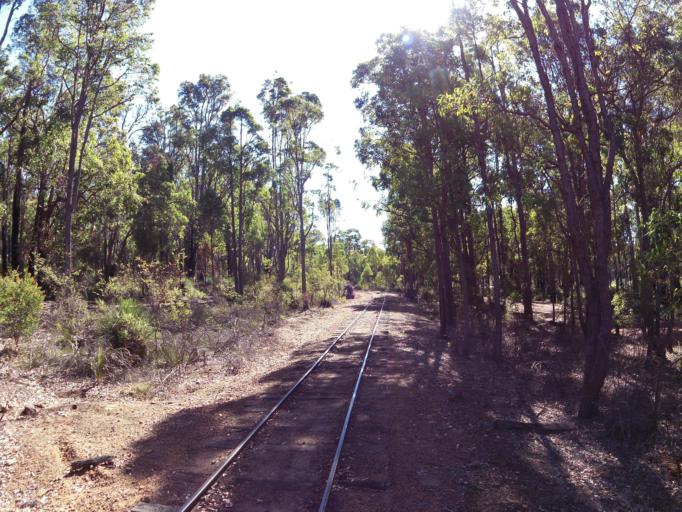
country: AU
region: Western Australia
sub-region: Waroona
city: Waroona
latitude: -32.7112
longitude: 116.0740
